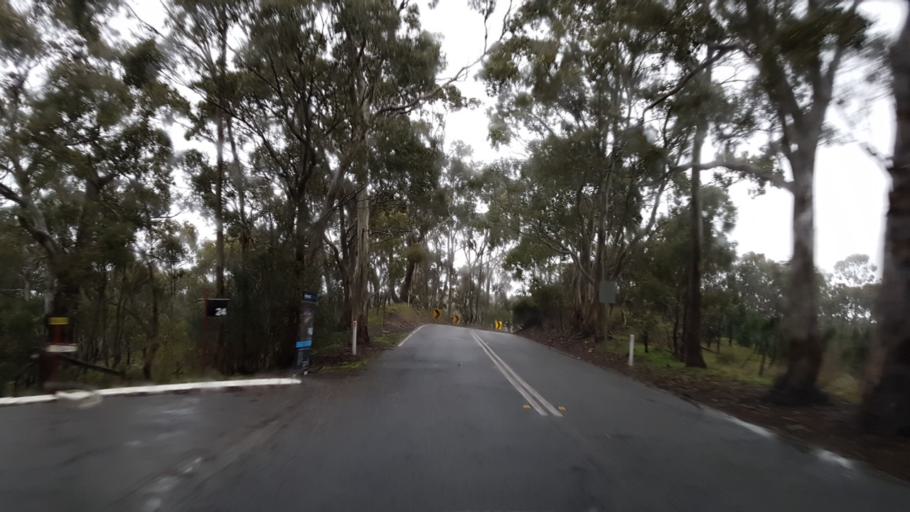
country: AU
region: South Australia
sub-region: Onkaparinga
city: Craigburn Farm
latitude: -35.0862
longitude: 138.6166
